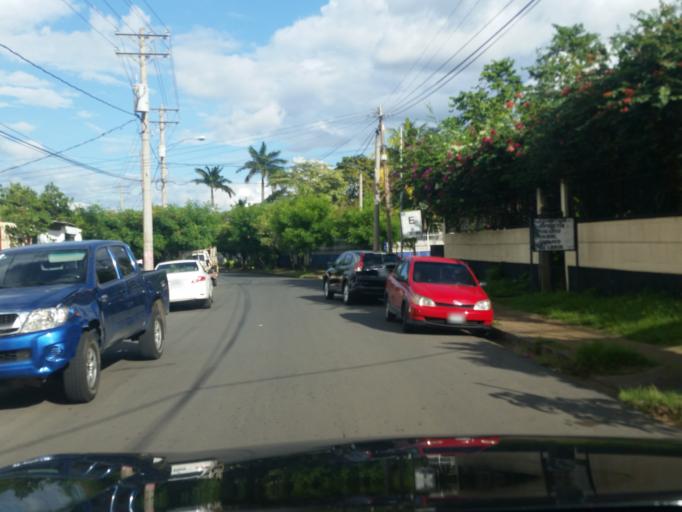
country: NI
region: Managua
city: Ciudad Sandino
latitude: 12.1262
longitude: -86.3090
